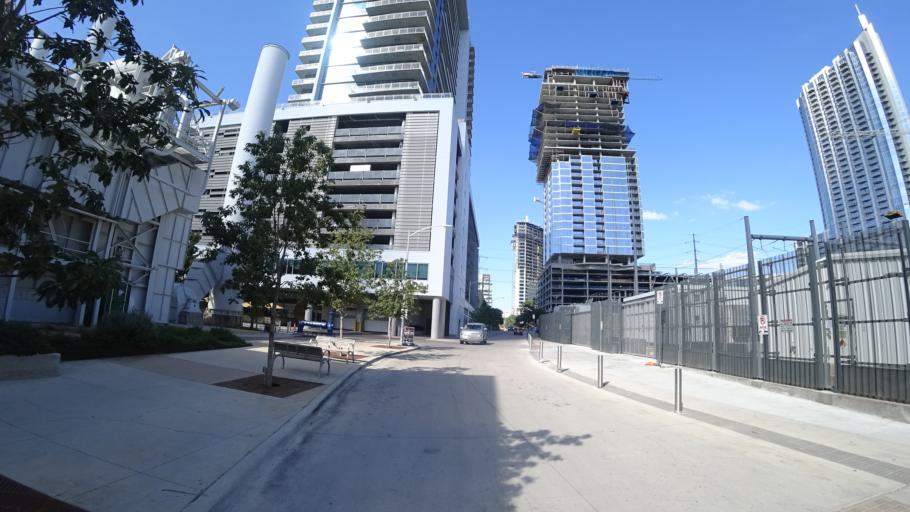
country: US
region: Texas
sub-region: Travis County
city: Austin
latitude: 30.2665
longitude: -97.7521
